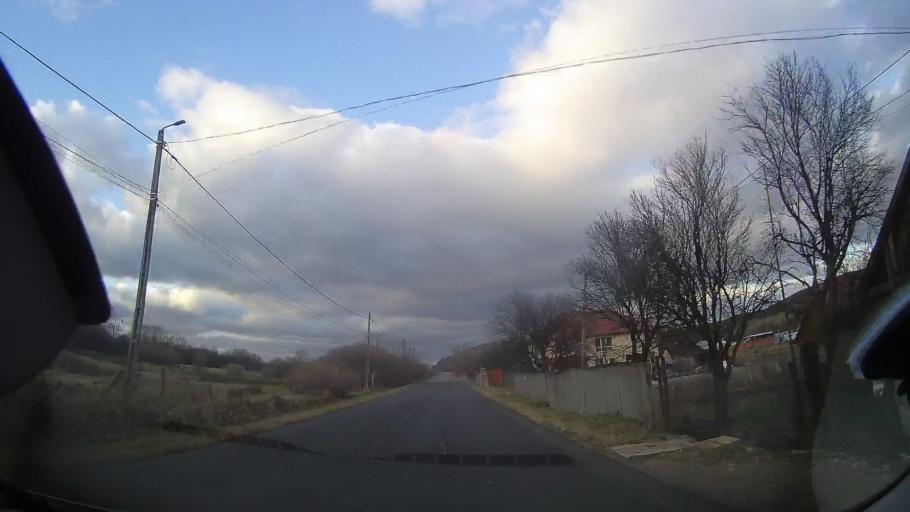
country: RO
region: Cluj
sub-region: Comuna Calatele
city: Calatele
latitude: 46.7768
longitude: 23.0066
